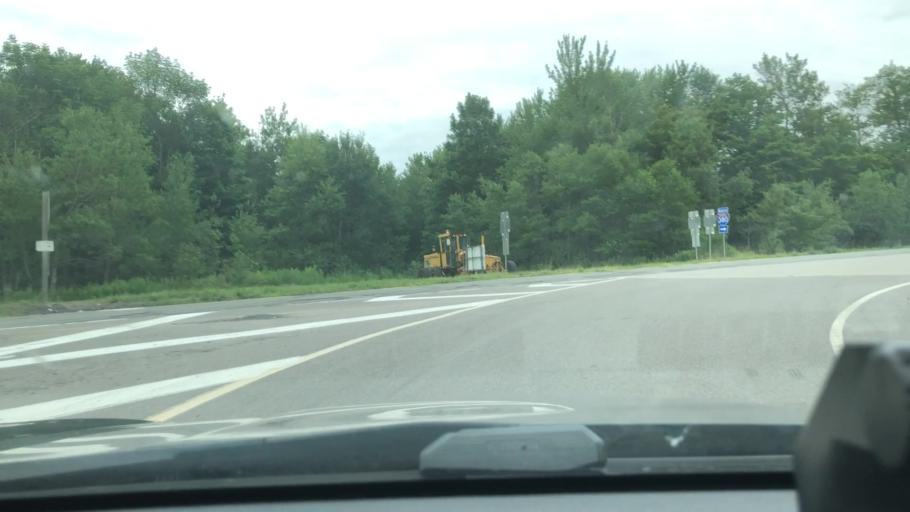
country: US
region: Pennsylvania
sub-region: Lackawanna County
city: Moscow
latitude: 41.2319
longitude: -75.4965
